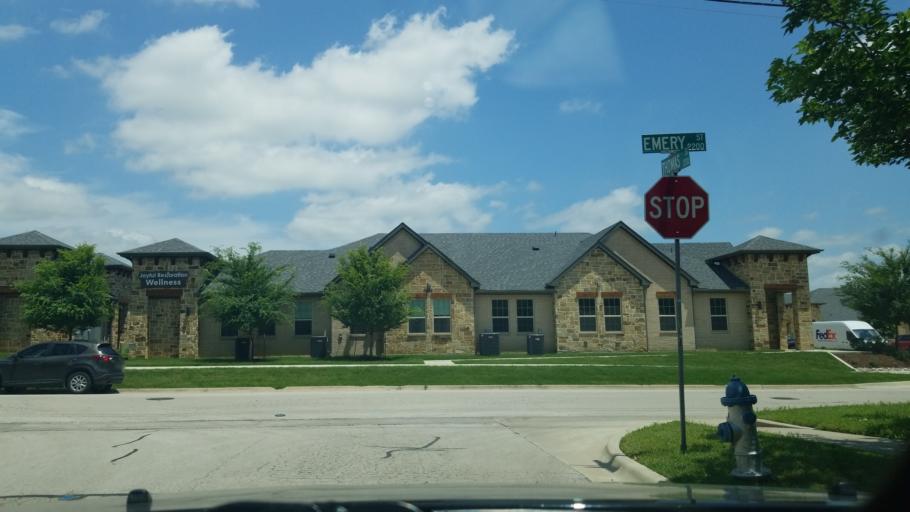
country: US
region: Texas
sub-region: Denton County
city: Denton
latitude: 33.2280
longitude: -97.1588
